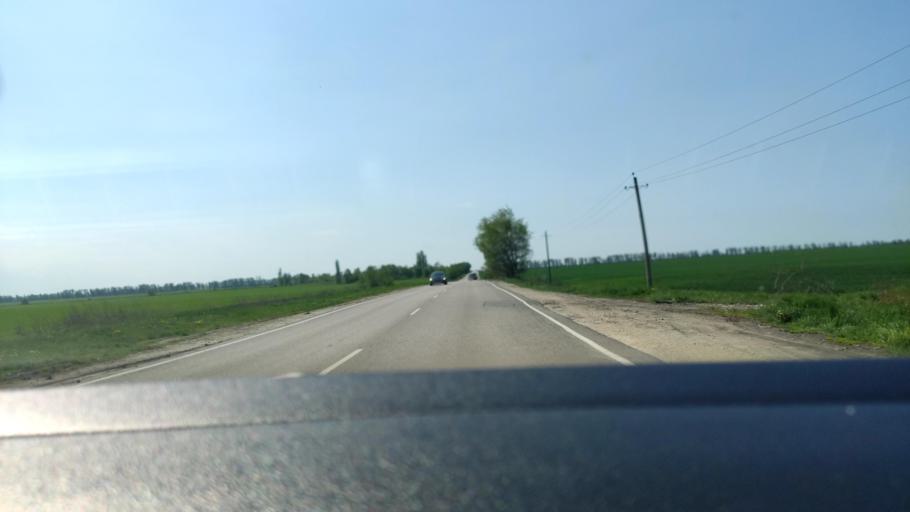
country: RU
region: Voronezj
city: Novaya Usman'
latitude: 51.5781
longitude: 39.3749
